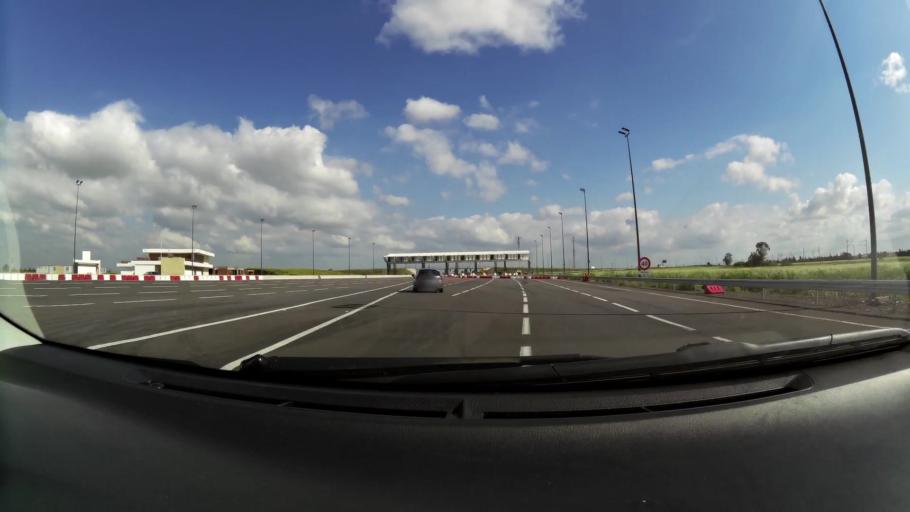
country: MA
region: Chaouia-Ouardigha
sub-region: Settat Province
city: Berrechid
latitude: 33.3199
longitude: -7.6044
